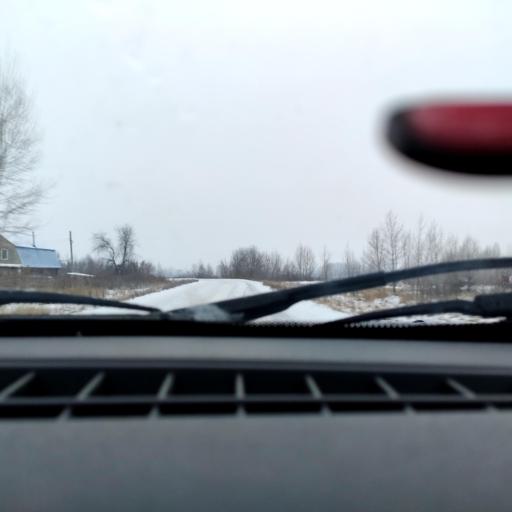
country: RU
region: Bashkortostan
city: Blagoveshchensk
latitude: 54.9039
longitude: 56.0127
